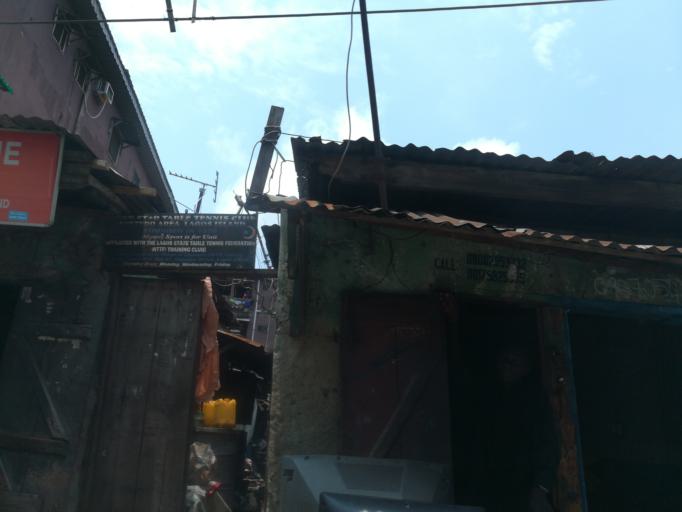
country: NG
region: Lagos
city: Lagos
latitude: 6.4557
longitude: 3.3980
